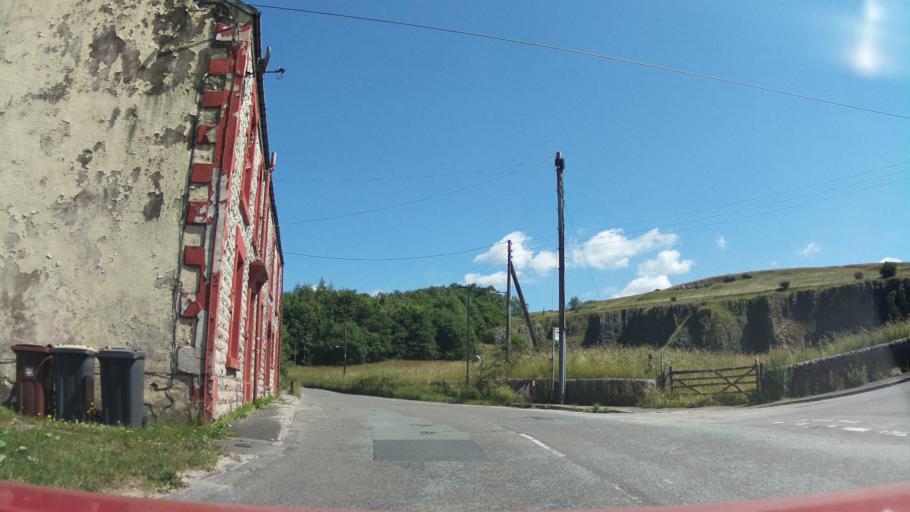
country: GB
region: England
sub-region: Derbyshire
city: Buxton
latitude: 53.2886
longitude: -1.8631
